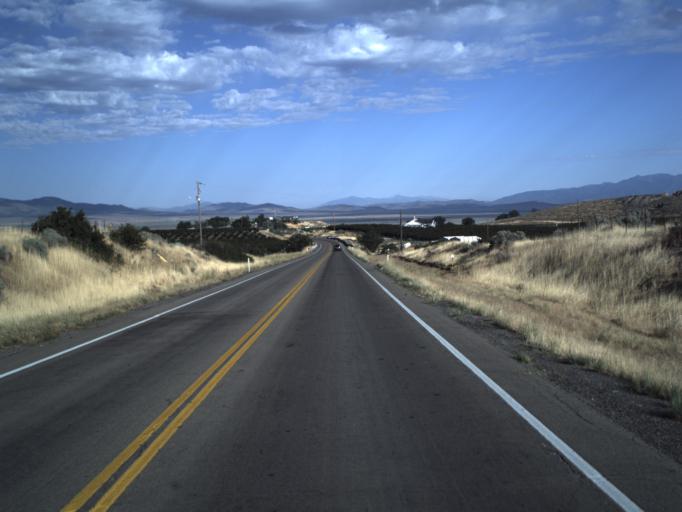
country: US
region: Utah
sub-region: Utah County
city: Santaquin
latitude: 39.9827
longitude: -111.8080
